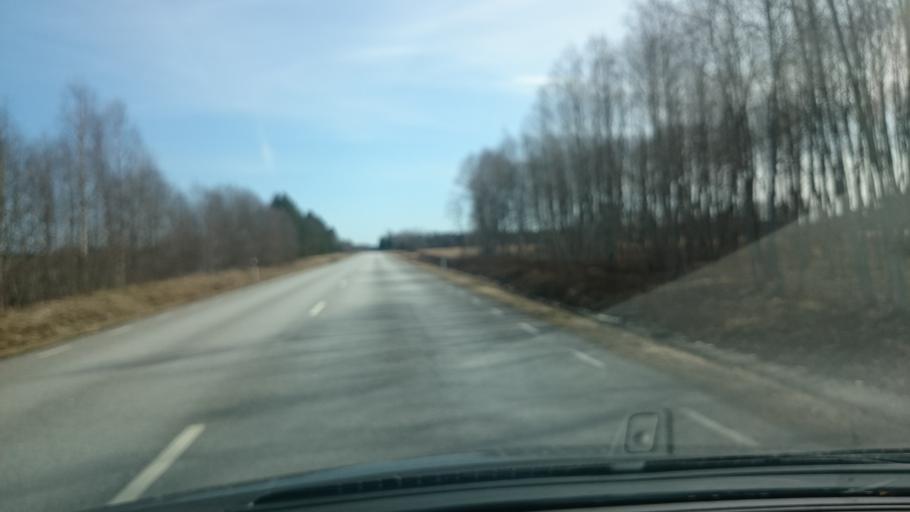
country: EE
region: Paernumaa
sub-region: Tootsi vald
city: Tootsi
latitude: 58.6553
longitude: 24.8405
